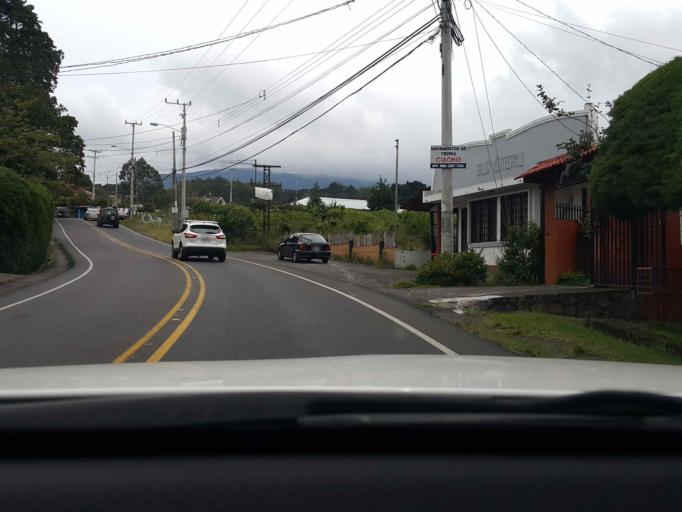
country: CR
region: Heredia
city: San Josecito
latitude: 10.0361
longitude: -84.0899
